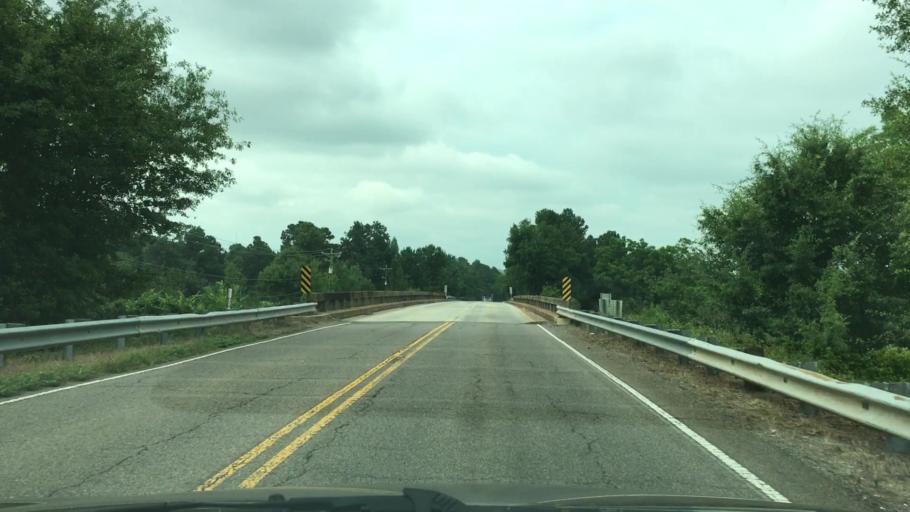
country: US
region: South Carolina
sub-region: Aiken County
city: Belvedere
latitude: 33.5495
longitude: -81.9577
